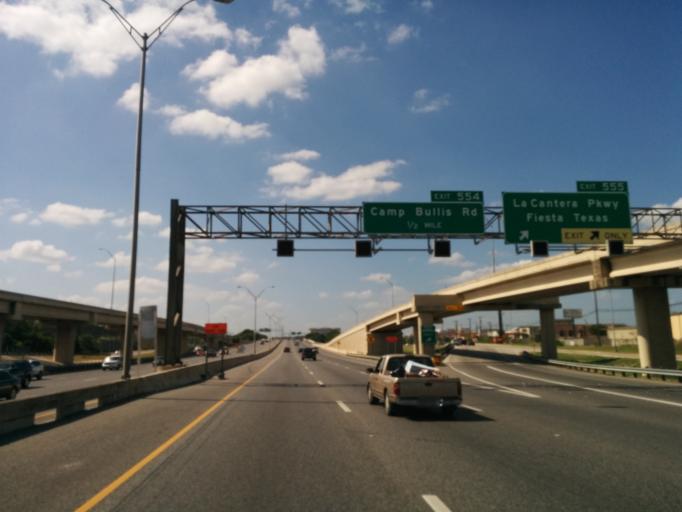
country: US
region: Texas
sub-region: Bexar County
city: Shavano Park
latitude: 29.6006
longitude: -98.6003
